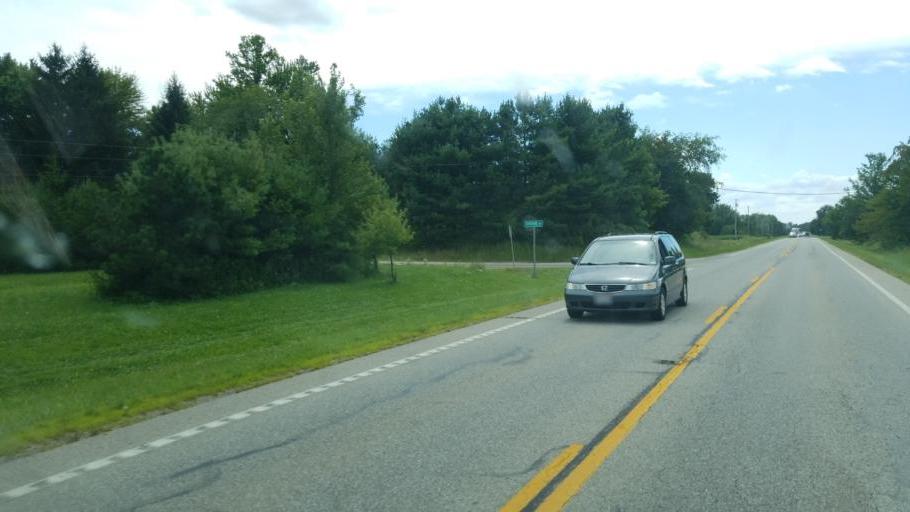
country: US
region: Ohio
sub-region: Knox County
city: Centerburg
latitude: 40.2687
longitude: -82.7744
